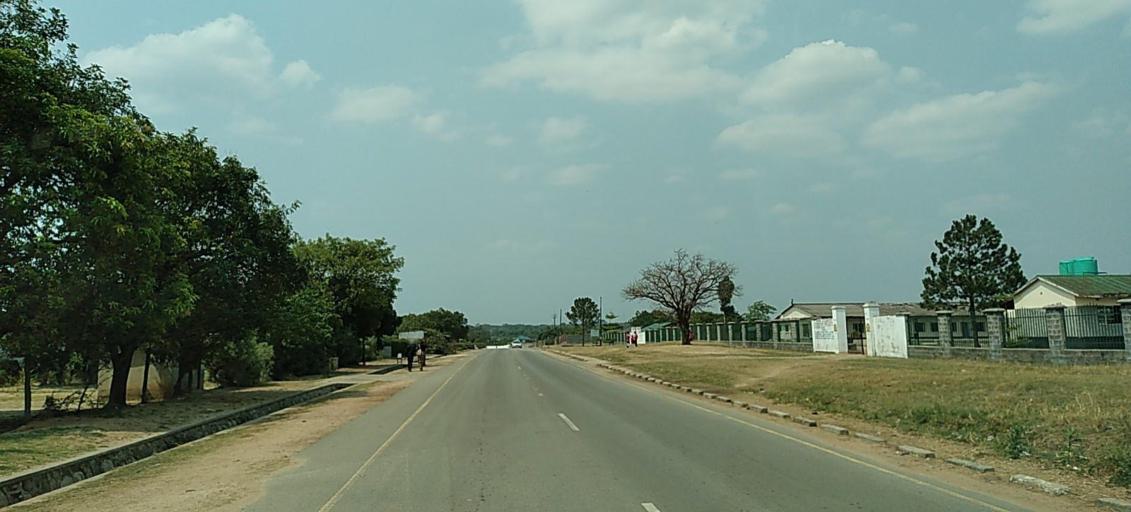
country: ZM
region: Copperbelt
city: Chambishi
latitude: -12.6324
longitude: 28.0588
